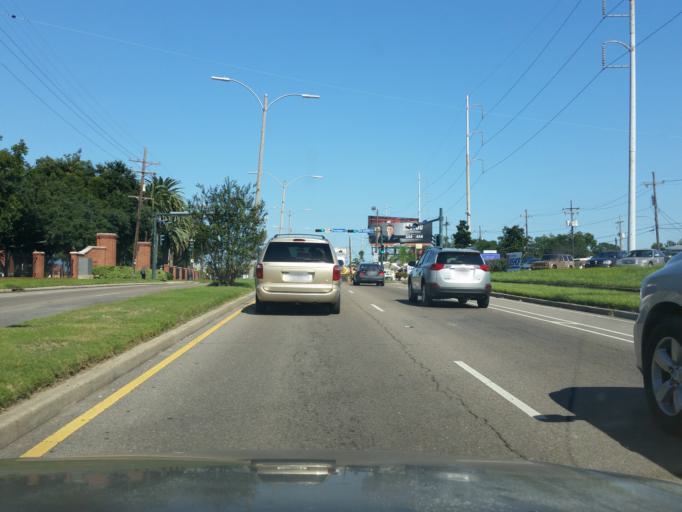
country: US
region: Louisiana
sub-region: Orleans Parish
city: New Orleans
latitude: 30.0027
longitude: -90.0451
